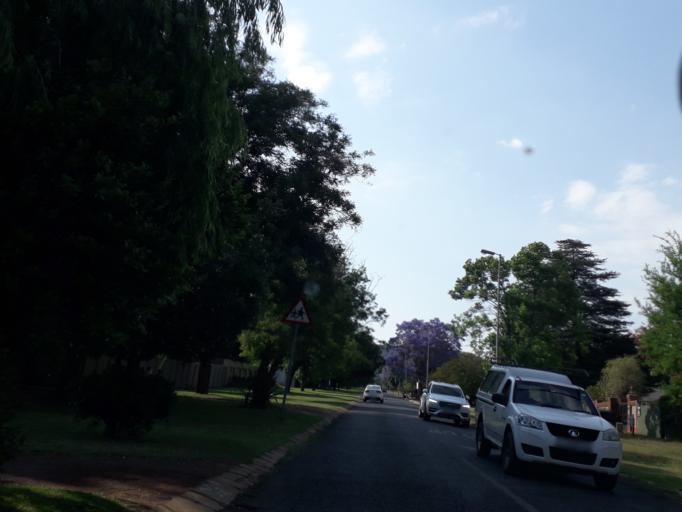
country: ZA
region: Gauteng
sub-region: City of Johannesburg Metropolitan Municipality
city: Roodepoort
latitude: -26.1264
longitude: 27.9574
